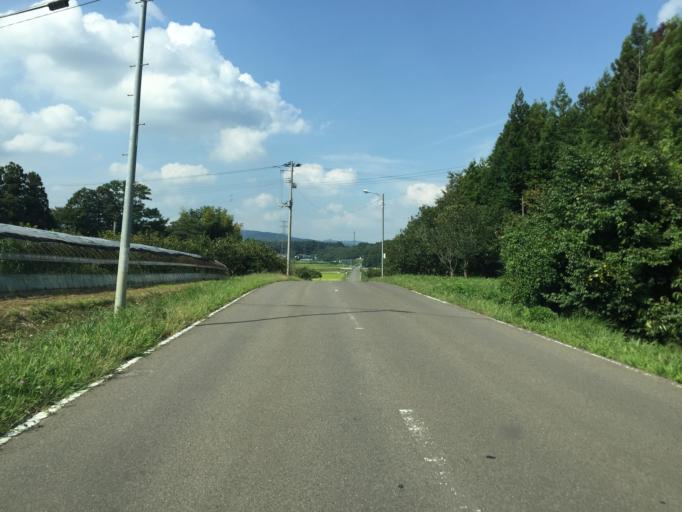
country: JP
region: Fukushima
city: Motomiya
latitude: 37.5616
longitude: 140.3839
